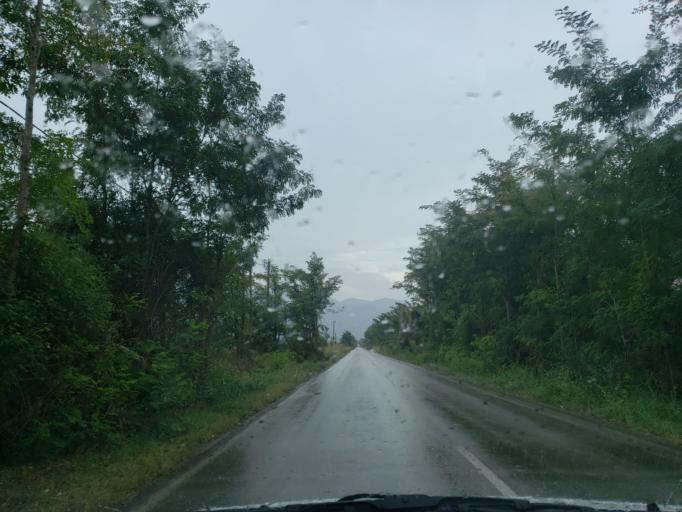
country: GR
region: Central Greece
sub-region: Nomos Fthiotidos
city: Anthili
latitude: 38.8391
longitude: 22.4411
